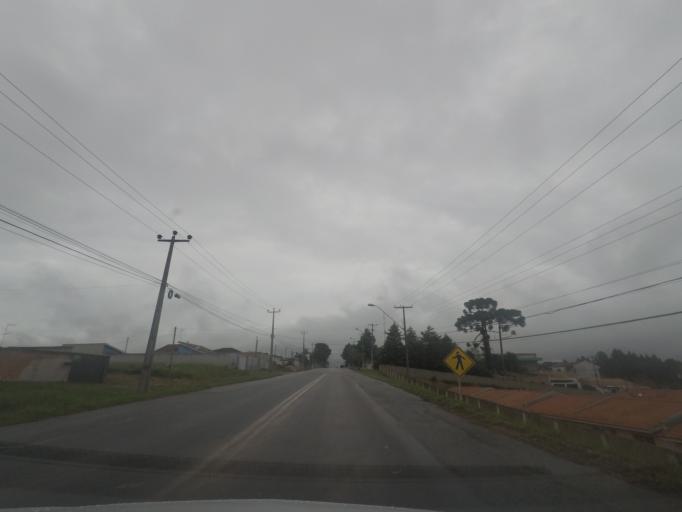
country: BR
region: Parana
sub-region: Campina Grande Do Sul
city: Campina Grande do Sul
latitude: -25.3285
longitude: -49.0781
